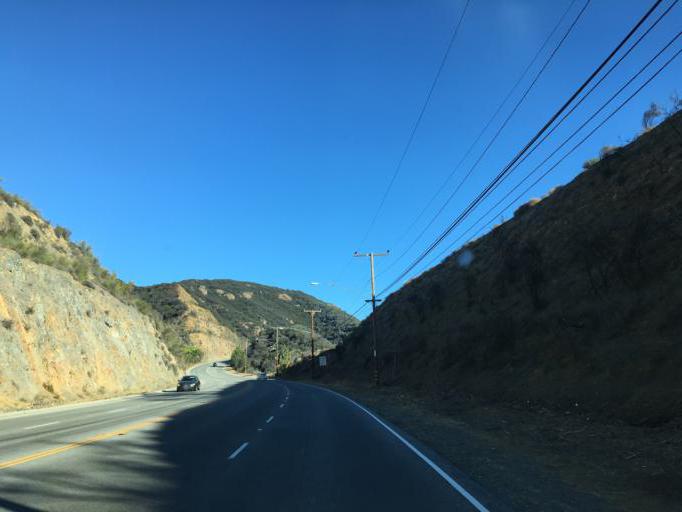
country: US
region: California
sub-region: Los Angeles County
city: Malibu
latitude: 34.0652
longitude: -118.8071
